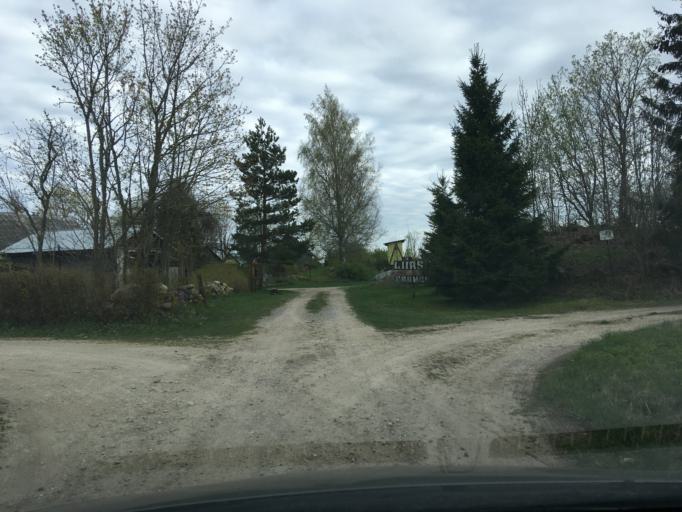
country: EE
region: Laeaene
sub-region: Lihula vald
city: Lihula
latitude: 58.5747
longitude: 23.7237
